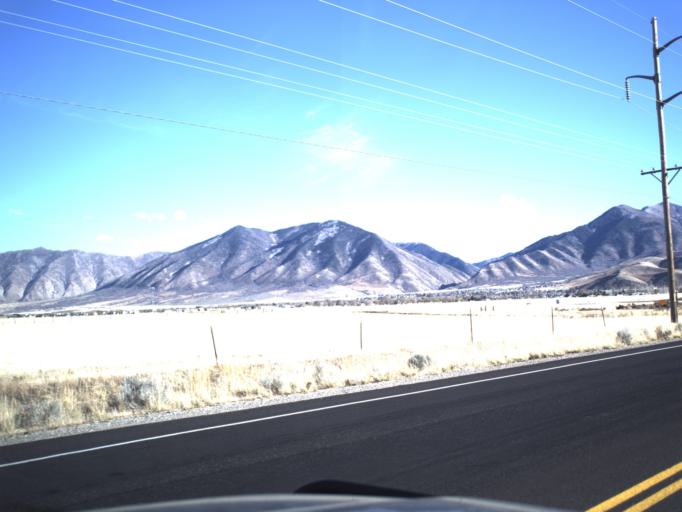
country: US
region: Utah
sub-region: Tooele County
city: Tooele
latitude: 40.5463
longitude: -112.3403
